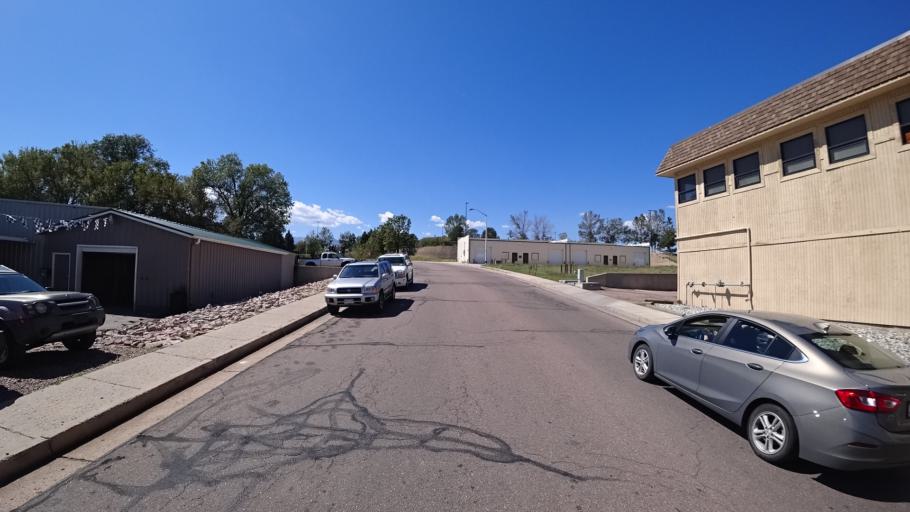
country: US
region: Colorado
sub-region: El Paso County
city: Colorado Springs
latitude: 38.8369
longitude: -104.7671
